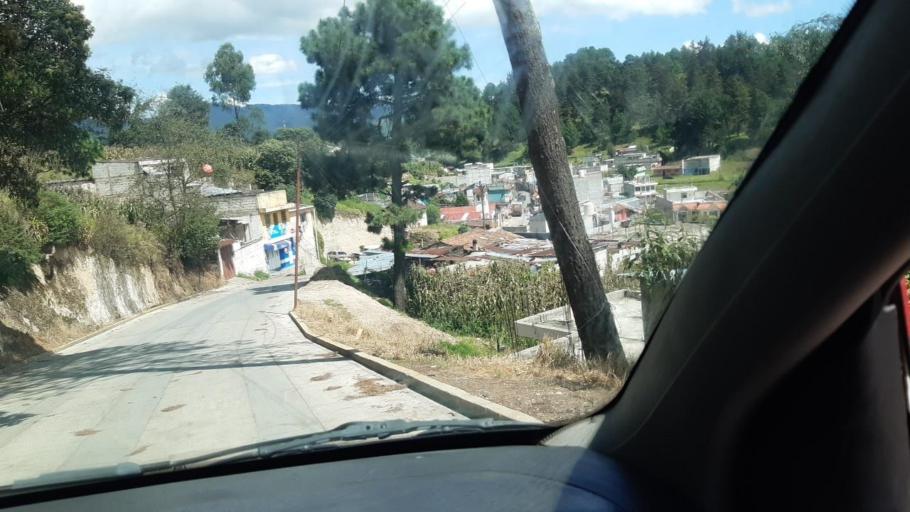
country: GT
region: Quetzaltenango
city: Salcaja
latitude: 14.8681
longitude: -91.4562
